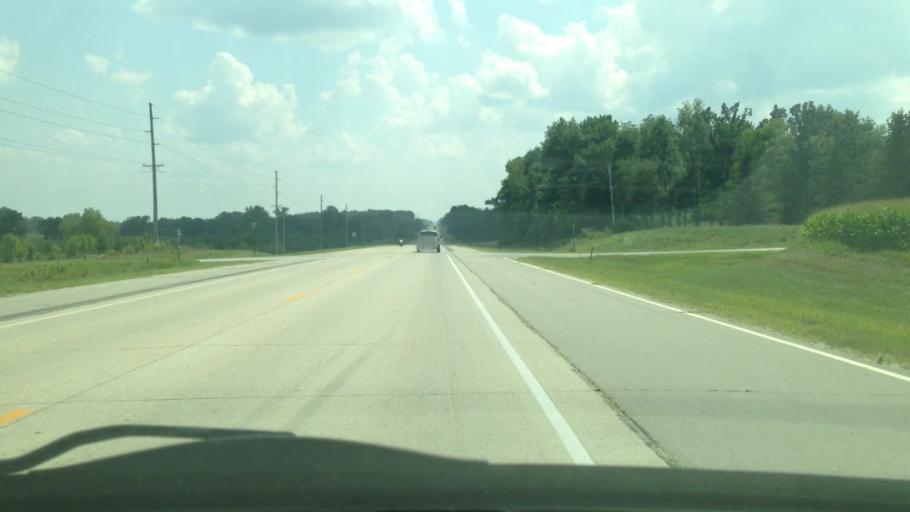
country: US
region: Minnesota
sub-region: Fillmore County
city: Spring Valley
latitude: 43.6318
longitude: -92.3901
